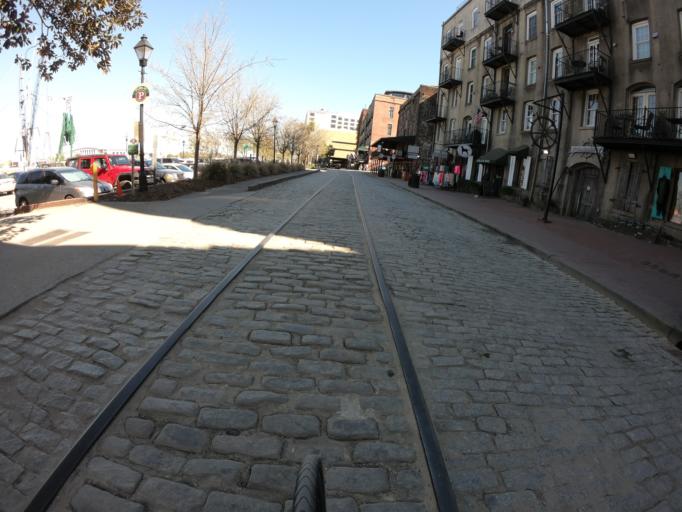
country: US
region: Georgia
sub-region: Chatham County
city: Savannah
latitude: 32.0826
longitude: -81.0938
